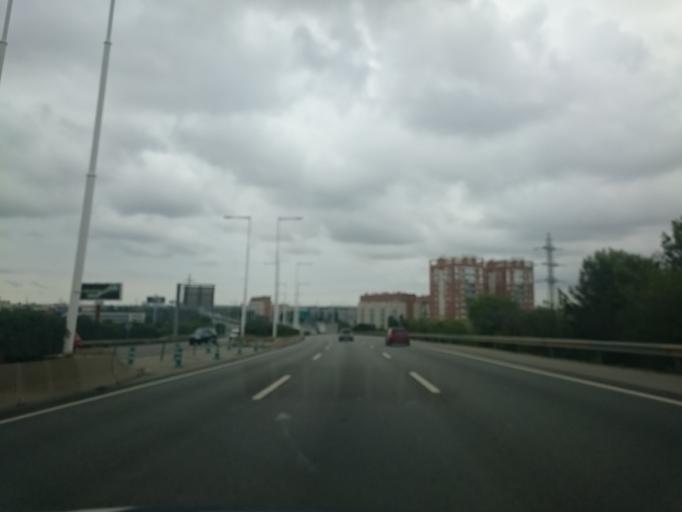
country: ES
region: Catalonia
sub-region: Provincia de Barcelona
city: Cornella de Llobregat
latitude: 41.3590
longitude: 2.0881
